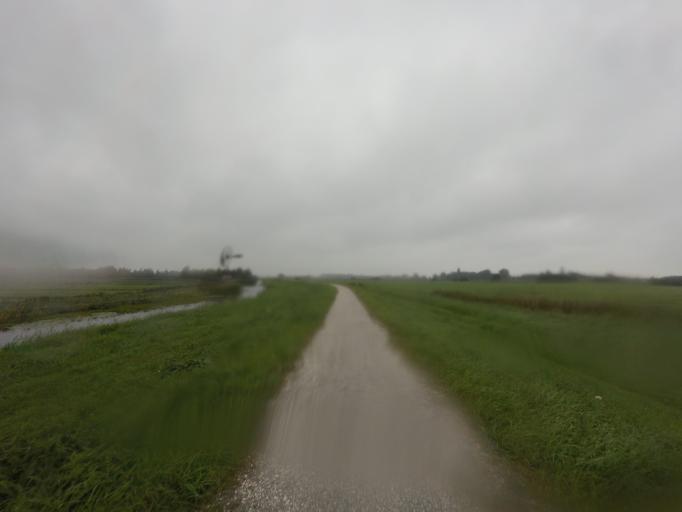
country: NL
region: Friesland
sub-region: Gemeente Smallingerland
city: Oudega
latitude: 53.1028
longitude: 5.9732
